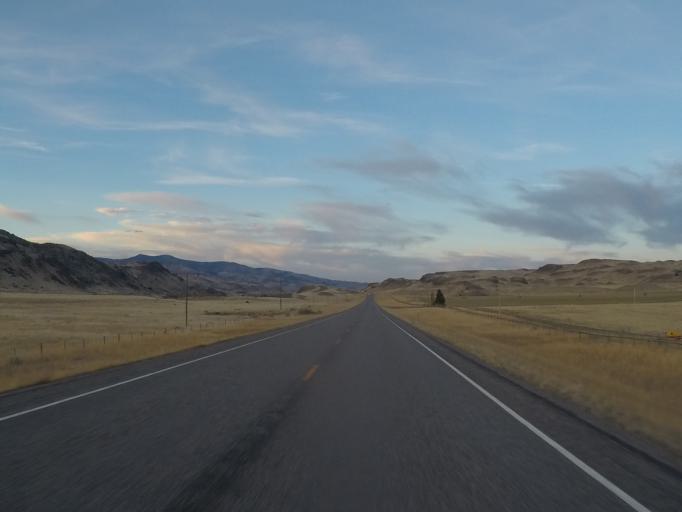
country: US
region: Montana
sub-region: Gallatin County
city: Bozeman
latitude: 45.2271
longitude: -110.8786
